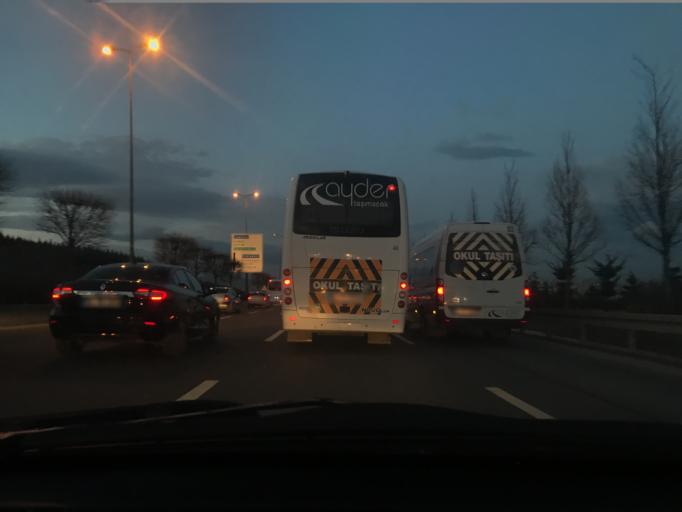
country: TR
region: Ankara
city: Batikent
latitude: 39.9240
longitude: 32.7763
